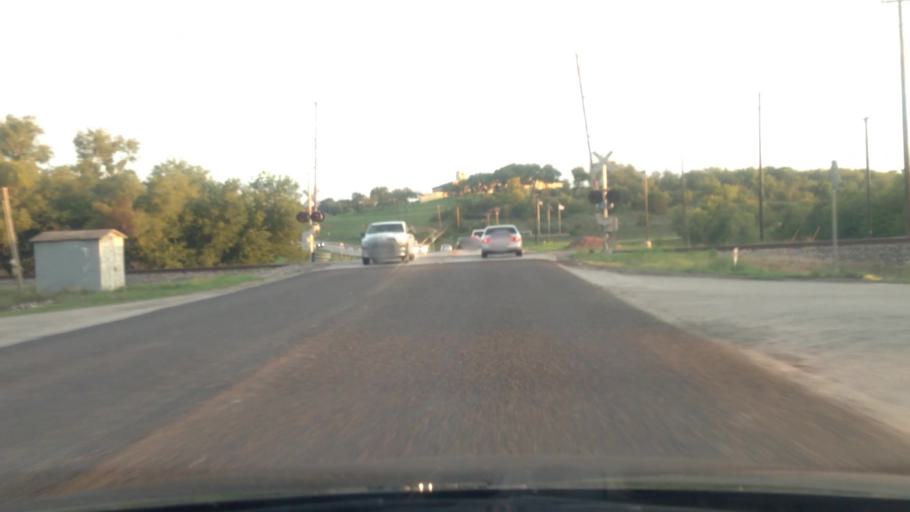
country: US
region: Texas
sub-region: Tarrant County
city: Benbrook
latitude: 32.6786
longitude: -97.4988
